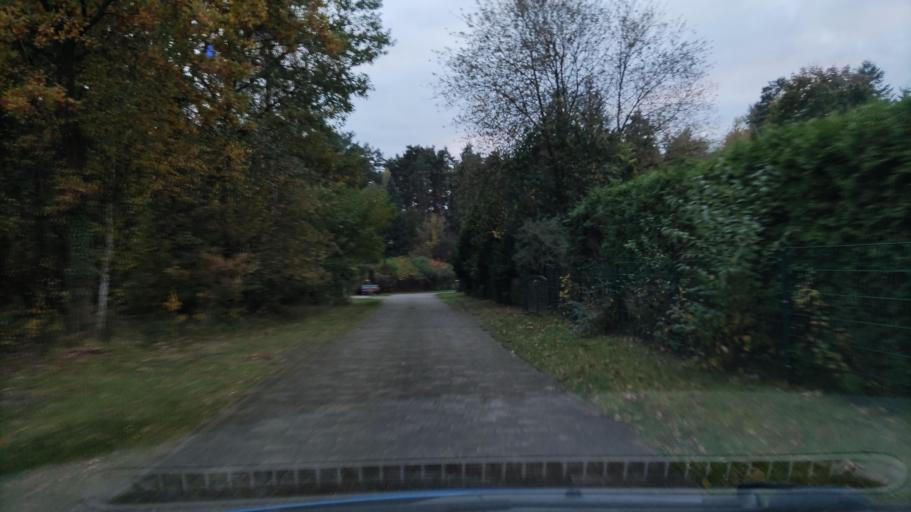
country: DE
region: Lower Saxony
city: Hitzacker
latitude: 53.1273
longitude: 11.0221
